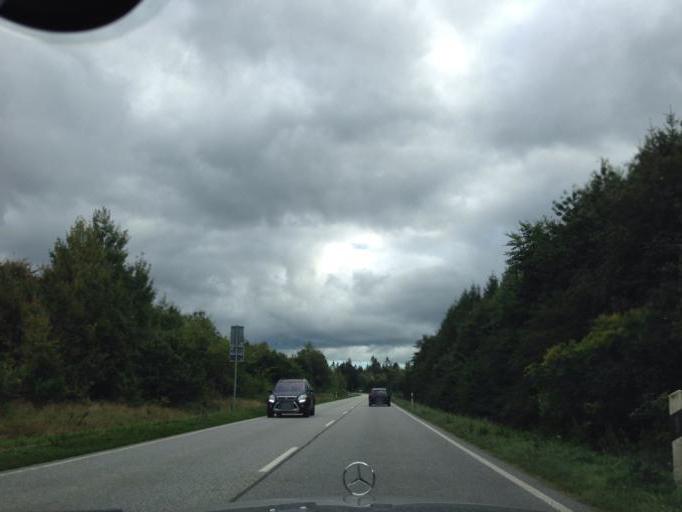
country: DE
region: Schleswig-Holstein
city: Leck
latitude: 54.7565
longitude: 8.9932
